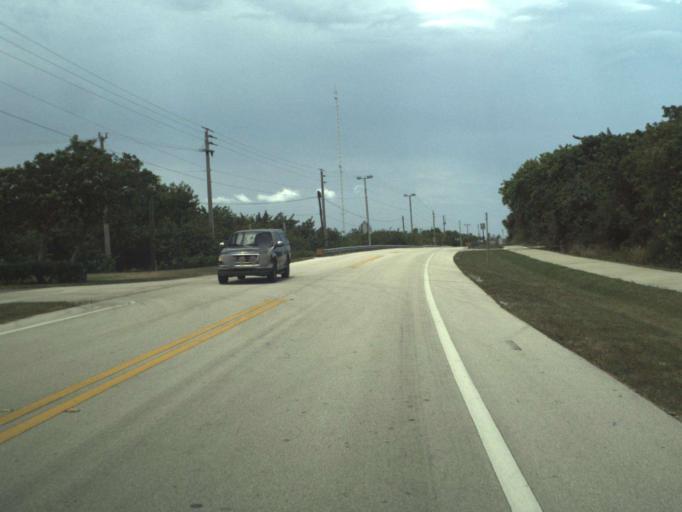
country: US
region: Florida
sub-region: Saint Lucie County
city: Hutchinson Island South
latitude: 27.3529
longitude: -80.2452
